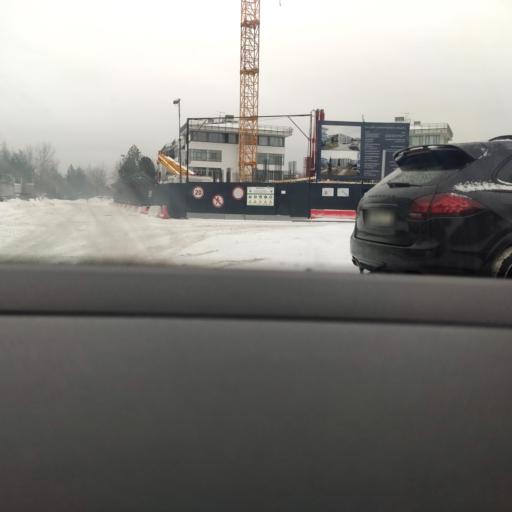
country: RU
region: Moskovskaya
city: Fili
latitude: 55.7594
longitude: 37.4498
